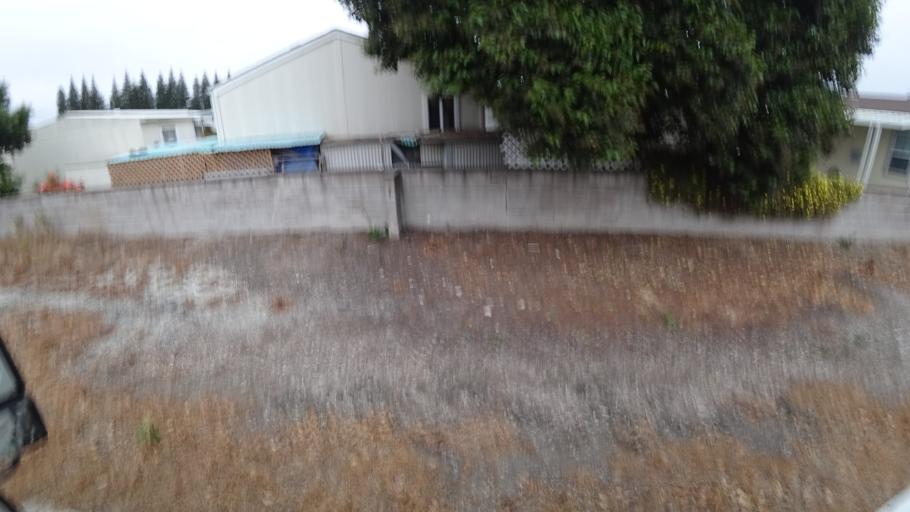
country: US
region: California
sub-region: Alameda County
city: Cherryland
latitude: 37.6507
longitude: -122.1156
